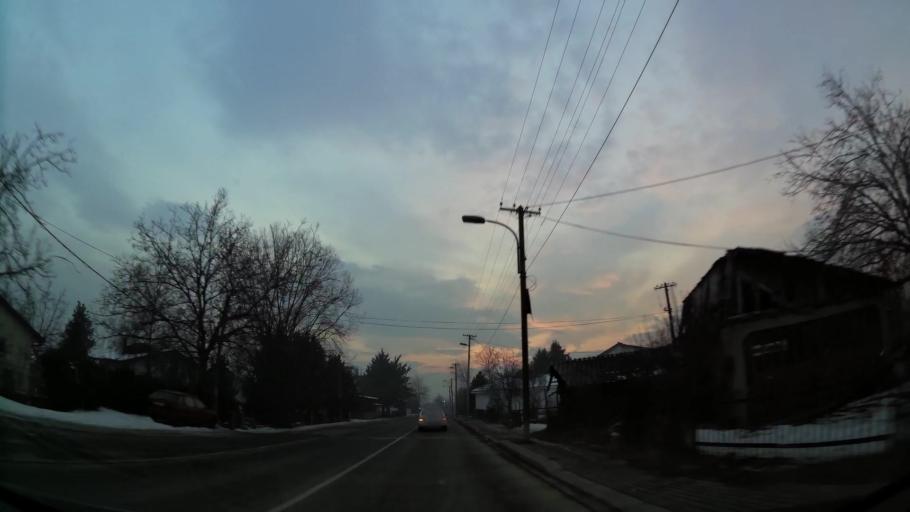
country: MK
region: Suto Orizari
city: Suto Orizare
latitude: 42.0143
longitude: 21.3924
